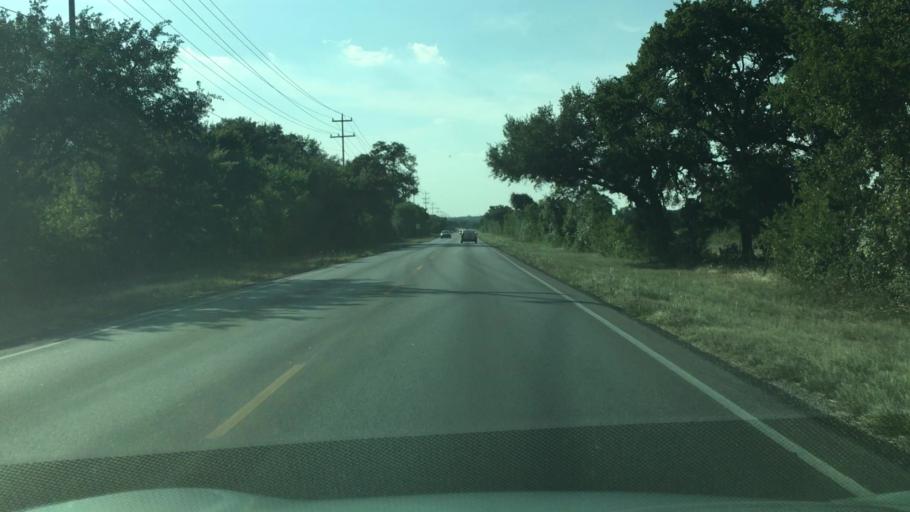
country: US
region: Texas
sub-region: Travis County
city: Shady Hollow
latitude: 30.1072
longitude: -97.9439
